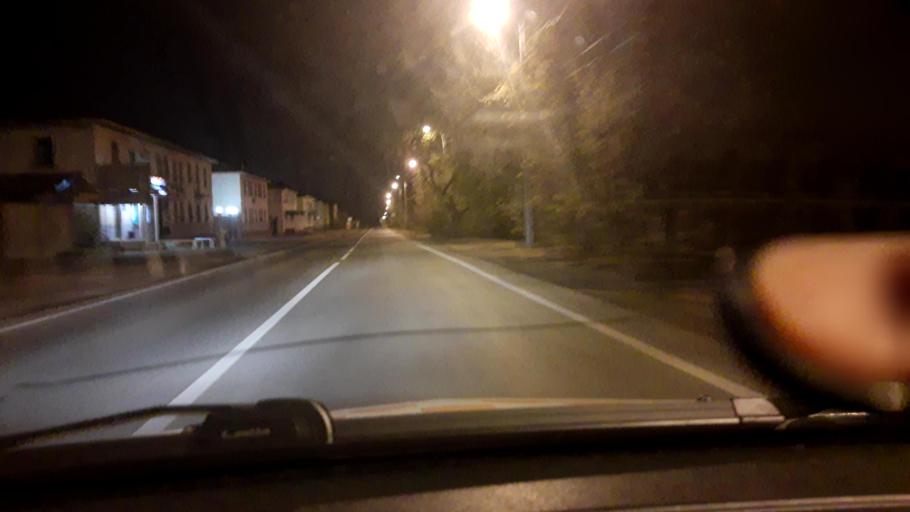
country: RU
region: Bashkortostan
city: Blagoveshchensk
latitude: 54.9023
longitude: 56.0535
